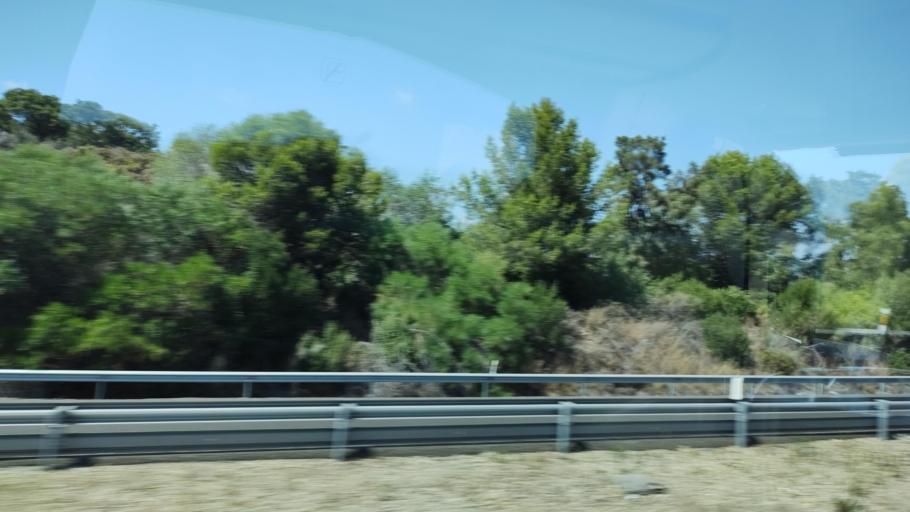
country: ES
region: Andalusia
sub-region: Provincia de Cadiz
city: San Roque
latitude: 36.2632
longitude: -5.3206
